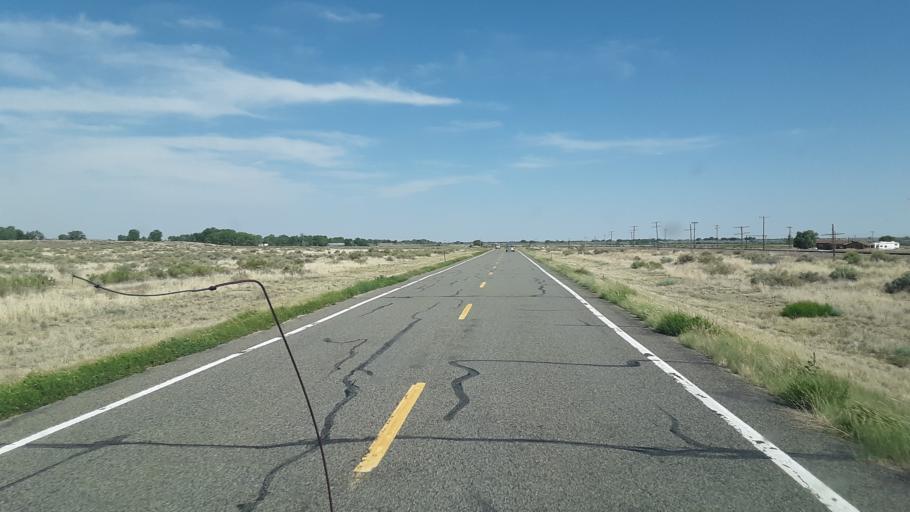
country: US
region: Colorado
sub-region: Otero County
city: Fowler
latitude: 38.2235
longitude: -104.2032
